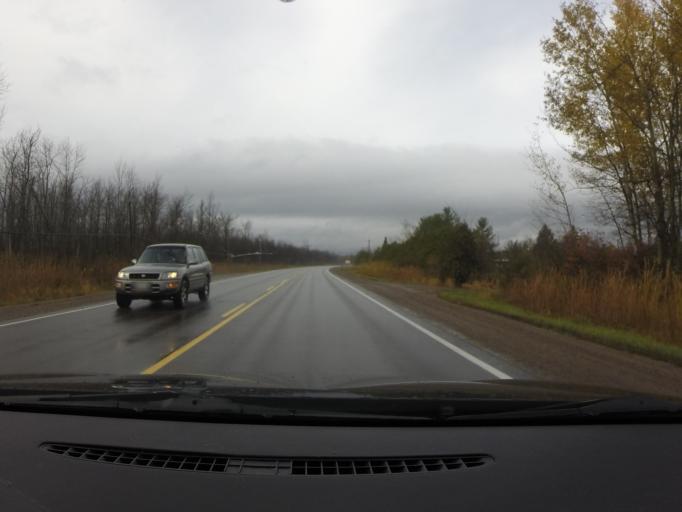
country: CA
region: Ontario
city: Belleville
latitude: 44.5568
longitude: -77.2794
